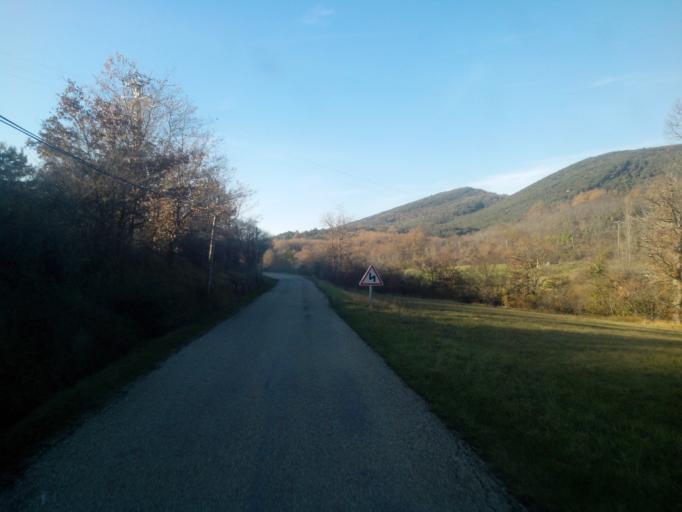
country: FR
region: Languedoc-Roussillon
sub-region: Departement des Pyrenees-Orientales
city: Saint-Paul-de-Fenouillet
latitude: 42.8619
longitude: 2.4580
